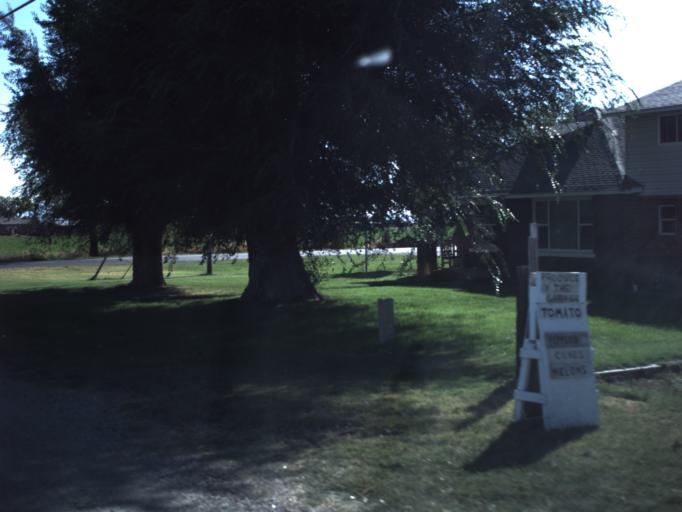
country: US
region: Utah
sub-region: Weber County
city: Hooper
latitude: 41.1569
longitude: -112.1229
